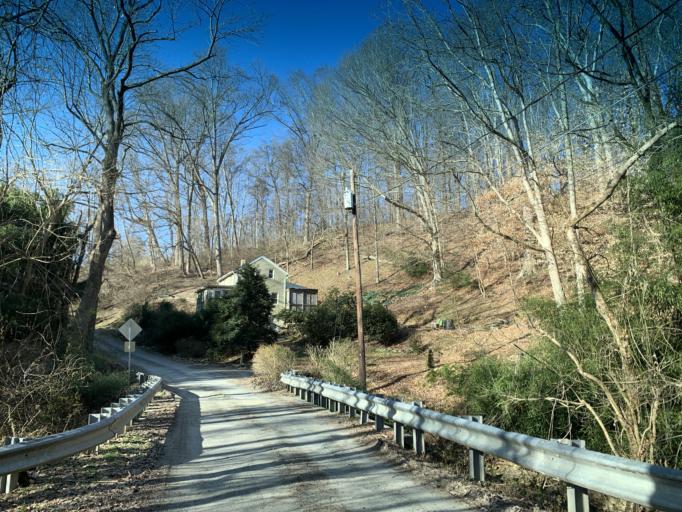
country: US
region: Maryland
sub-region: Harford County
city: Aberdeen
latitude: 39.6110
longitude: -76.2178
